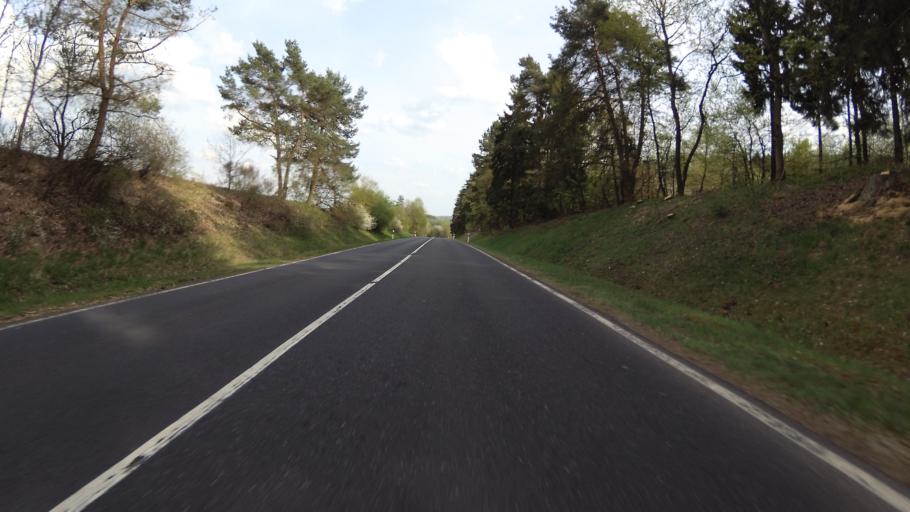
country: DE
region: Rheinland-Pfalz
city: Berenbach
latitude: 50.2302
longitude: 6.9457
